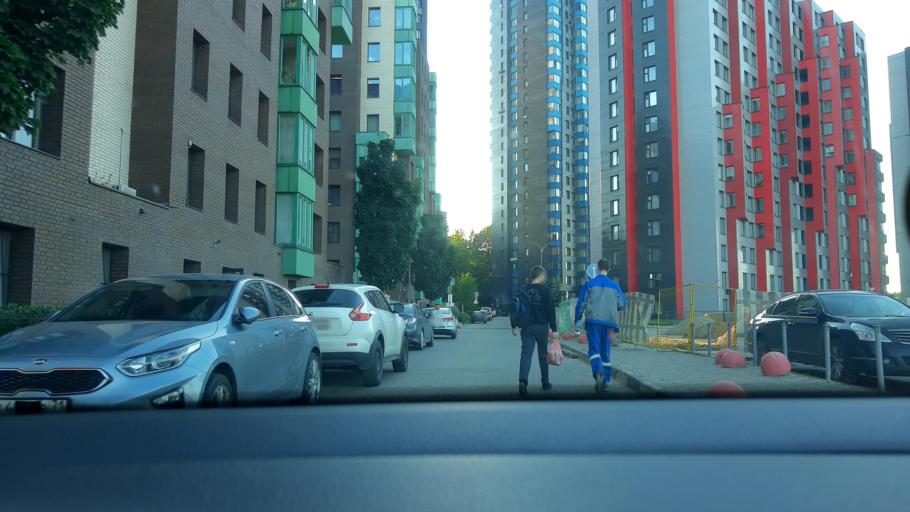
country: RU
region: Moskovskaya
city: Firsanovka
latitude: 55.9428
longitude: 37.2630
